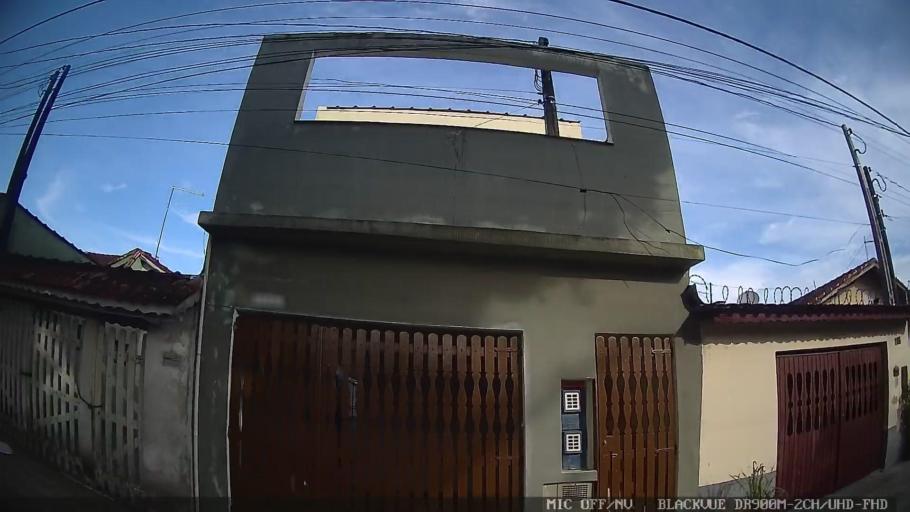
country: BR
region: Sao Paulo
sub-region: Itanhaem
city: Itanhaem
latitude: -24.1577
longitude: -46.7542
